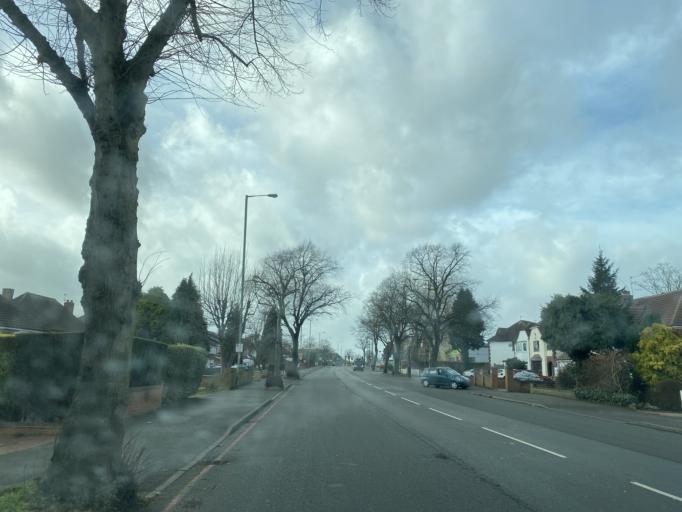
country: GB
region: England
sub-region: Walsall
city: Walsall
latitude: 52.5679
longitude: -1.9765
